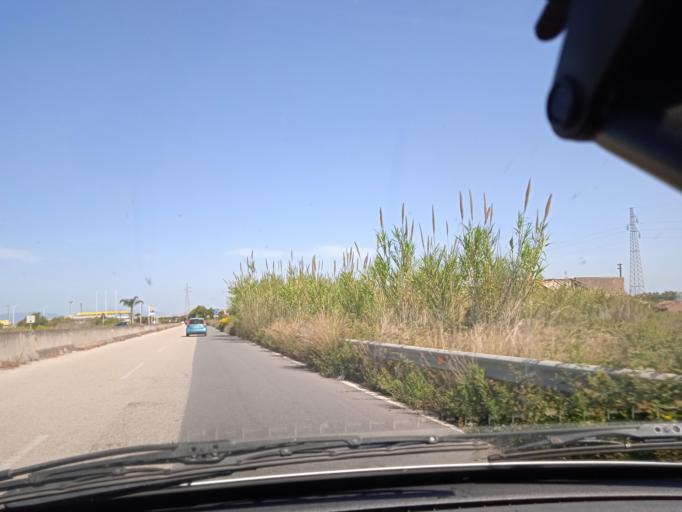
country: IT
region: Sicily
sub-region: Messina
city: San Filippo del Mela
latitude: 38.1909
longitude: 15.2604
